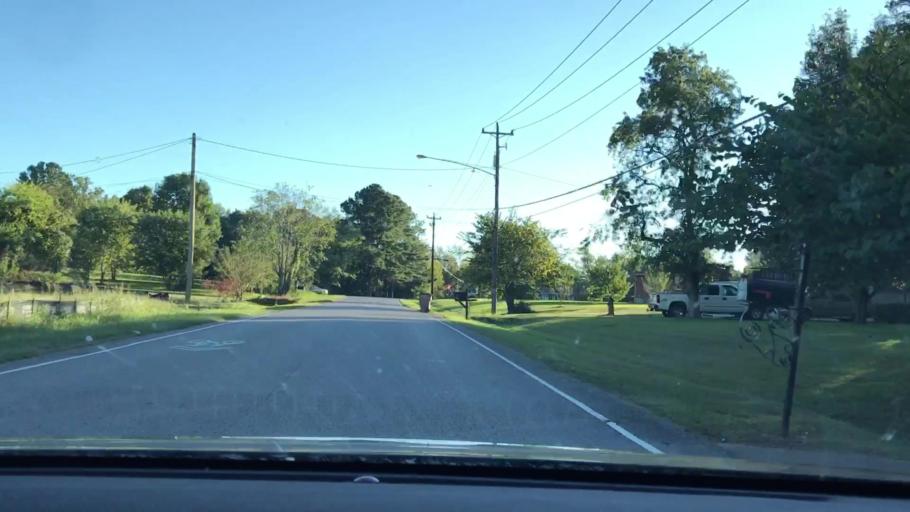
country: US
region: Tennessee
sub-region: Williamson County
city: Brentwood Estates
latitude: 36.0571
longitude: -86.7026
